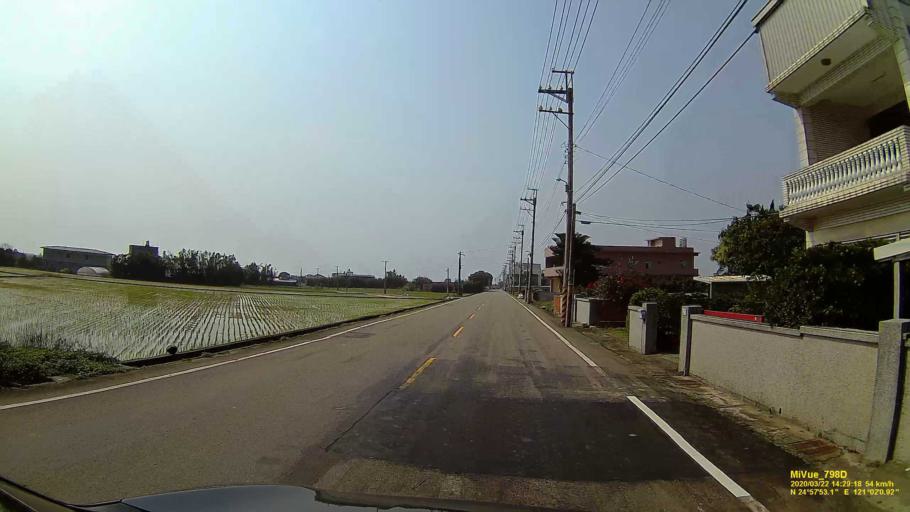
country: TW
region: Taiwan
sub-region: Hsinchu
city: Zhubei
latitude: 24.9650
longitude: 121.0330
